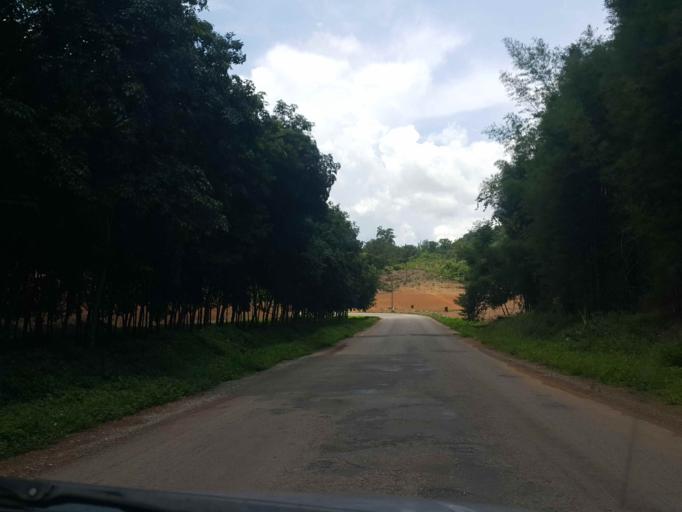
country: TH
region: Phayao
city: Chiang Muan
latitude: 18.9006
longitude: 100.1260
